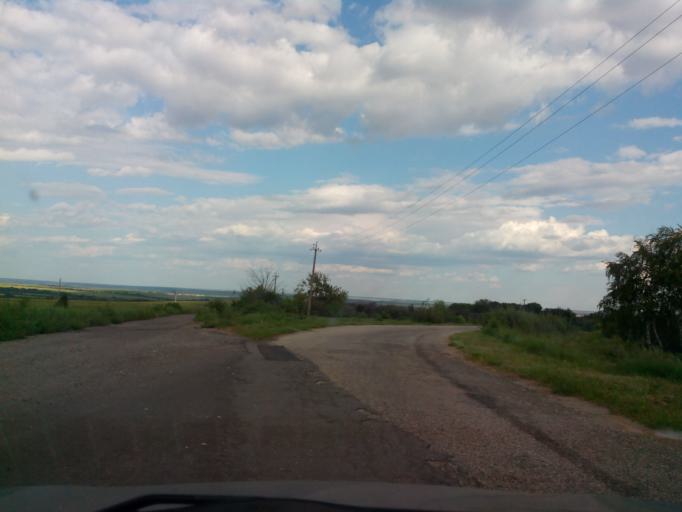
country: RU
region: Volgograd
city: Slashchevskaya
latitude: 49.7955
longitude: 42.4158
